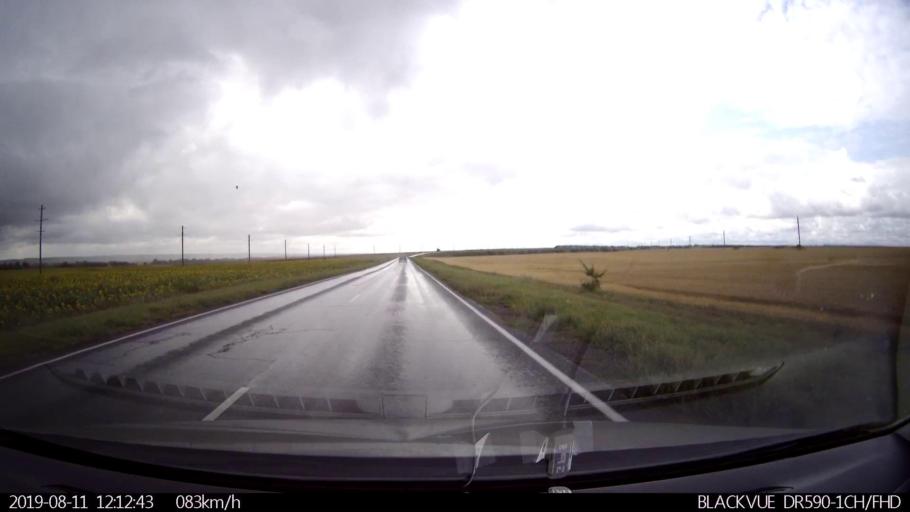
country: RU
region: Ulyanovsk
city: Silikatnyy
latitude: 53.9695
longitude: 47.9953
